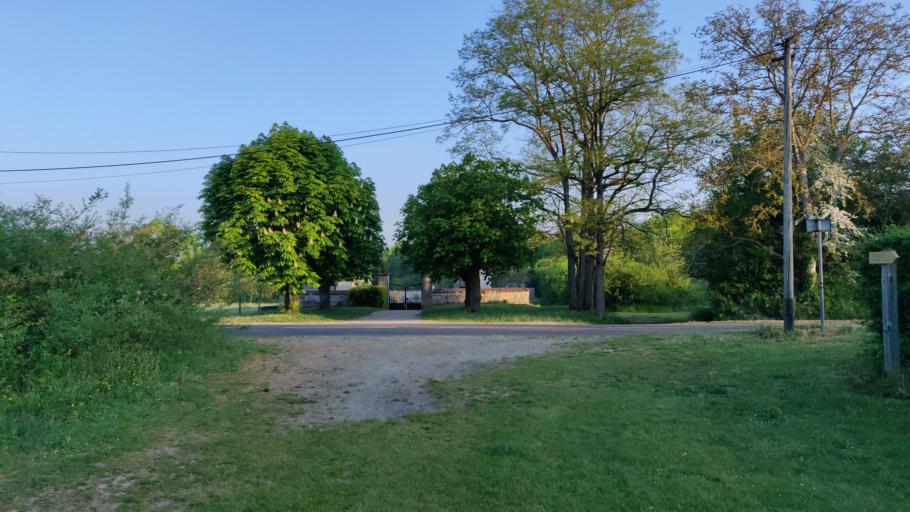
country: FR
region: Ile-de-France
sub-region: Departement des Yvelines
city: Freneuse
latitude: 49.0391
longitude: 1.6307
